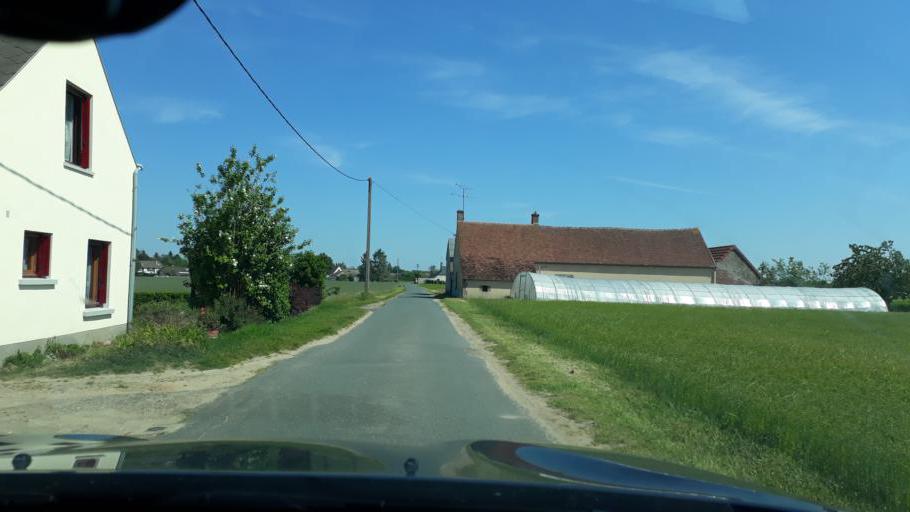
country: FR
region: Centre
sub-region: Departement du Loiret
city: Saint-Benoit-sur-Loire
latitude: 47.8068
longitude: 2.2625
